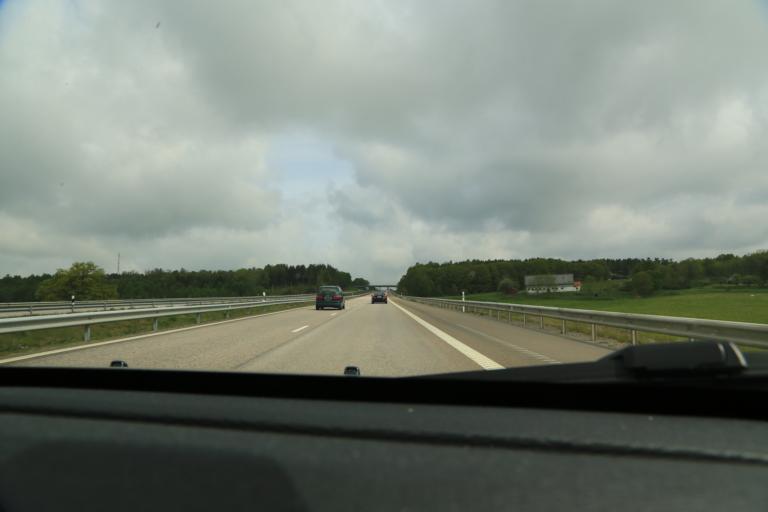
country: SE
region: Halland
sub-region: Kungsbacka Kommun
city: Frillesas
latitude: 57.2643
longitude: 12.2159
